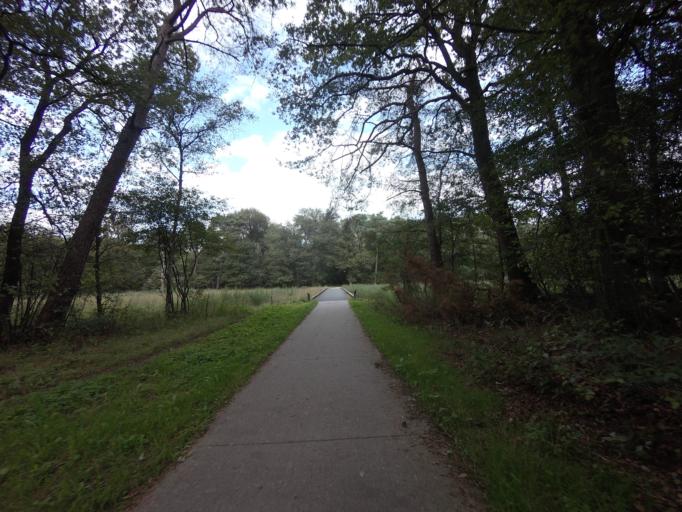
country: NL
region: Drenthe
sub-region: Gemeente Westerveld
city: Dwingeloo
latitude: 52.8119
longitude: 6.3555
